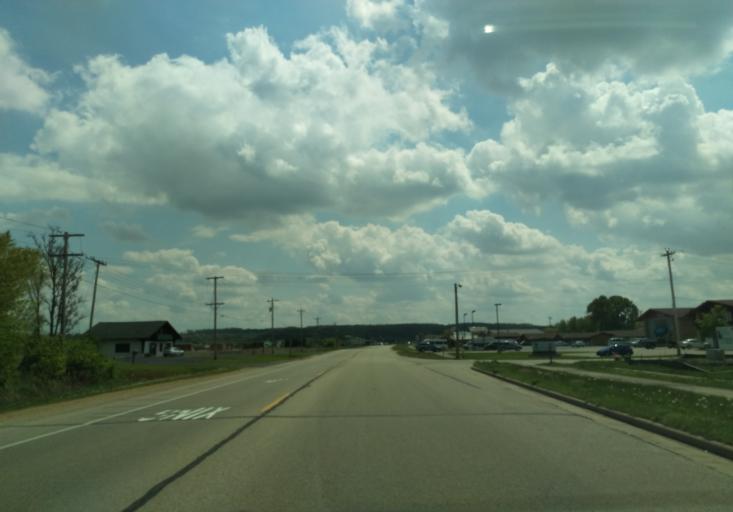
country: US
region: Wisconsin
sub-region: Green County
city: New Glarus
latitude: 42.8105
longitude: -89.6313
